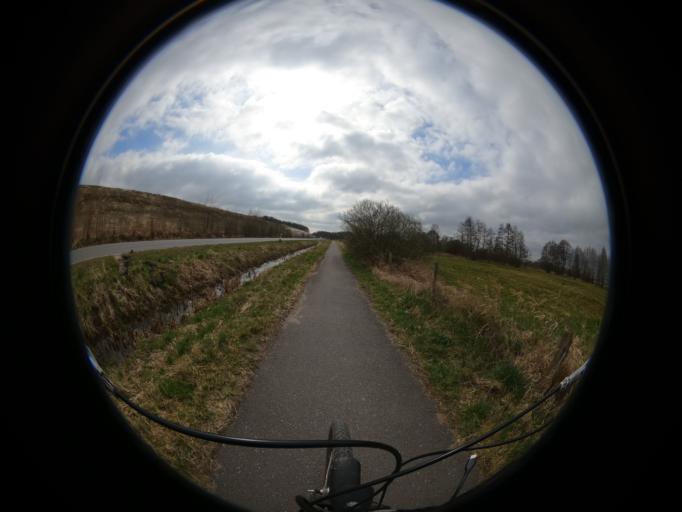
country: DE
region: Lower Saxony
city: Neu Wulmstorf
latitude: 53.4873
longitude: 9.7806
